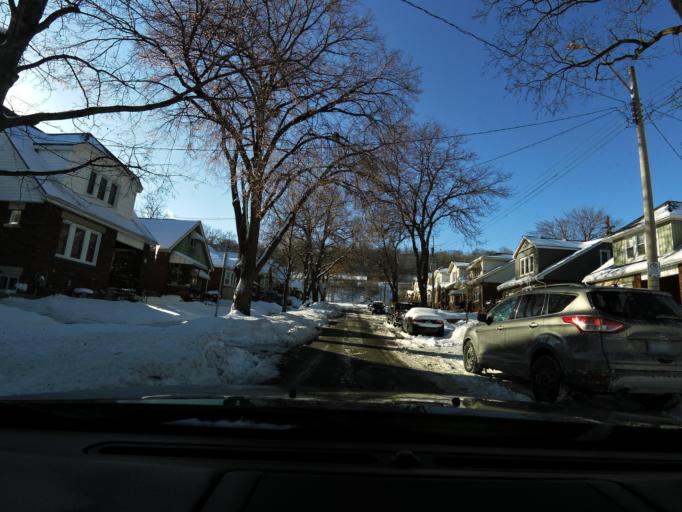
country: CA
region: Ontario
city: Hamilton
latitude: 43.2342
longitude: -79.8199
